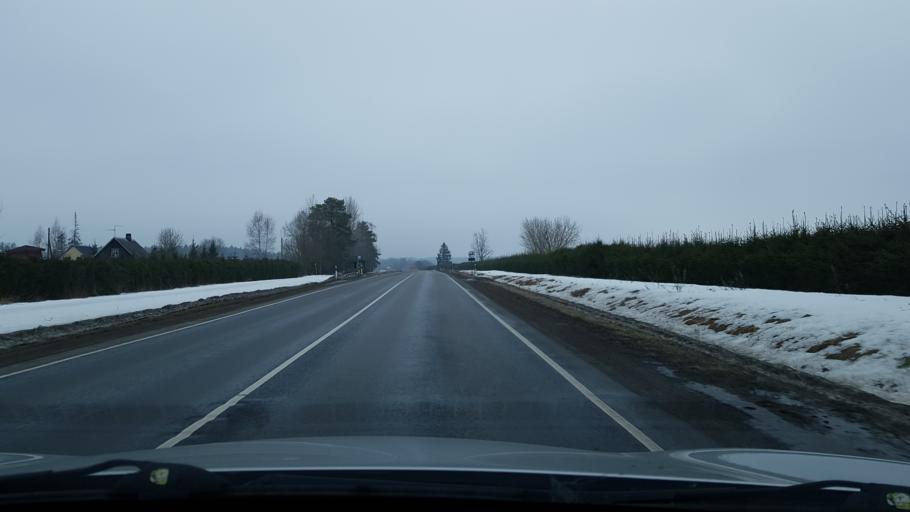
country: EE
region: Valgamaa
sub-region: Valga linn
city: Valga
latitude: 57.8360
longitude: 26.1248
